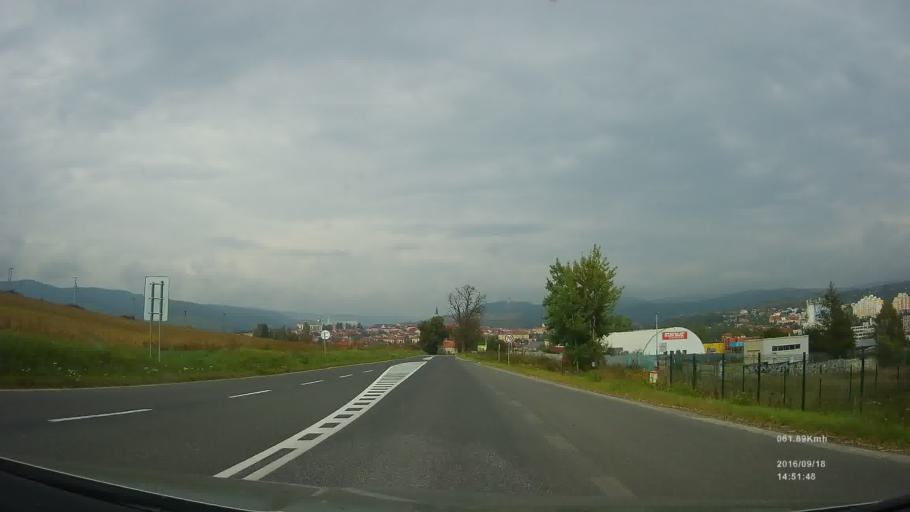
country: SK
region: Presovsky
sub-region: Okres Presov
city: Levoca
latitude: 49.0123
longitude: 20.5863
